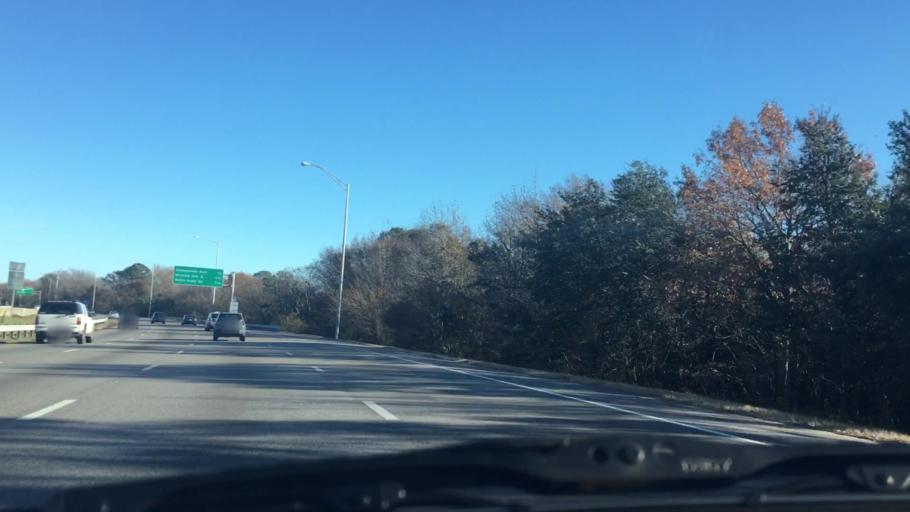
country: US
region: Virginia
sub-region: City of Norfolk
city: Norfolk
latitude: 36.9036
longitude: -76.2518
